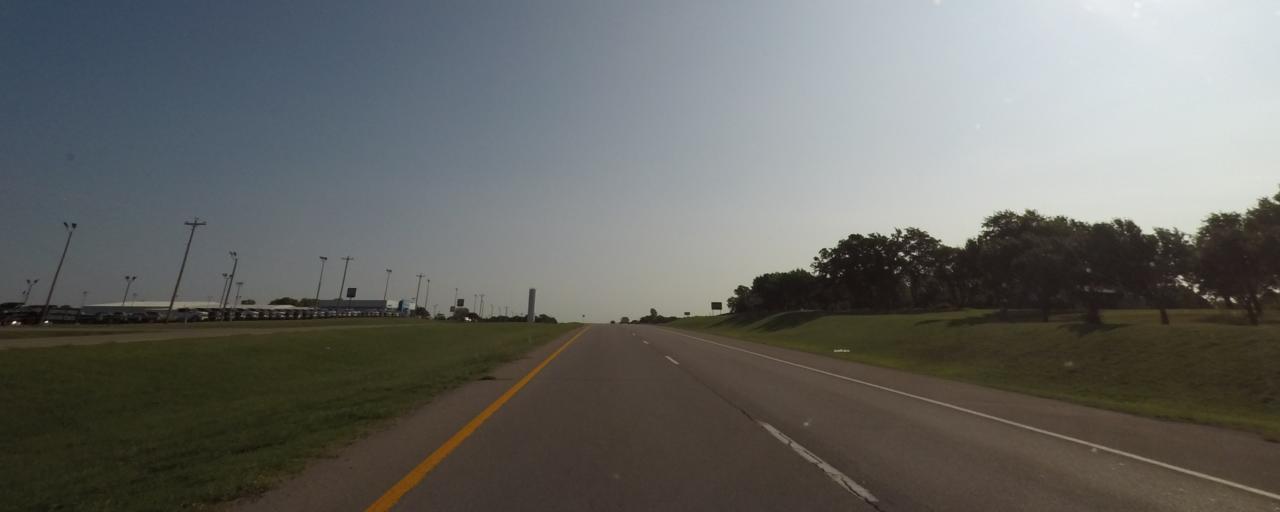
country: US
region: Oklahoma
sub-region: McClain County
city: Blanchard
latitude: 35.1474
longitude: -97.6392
